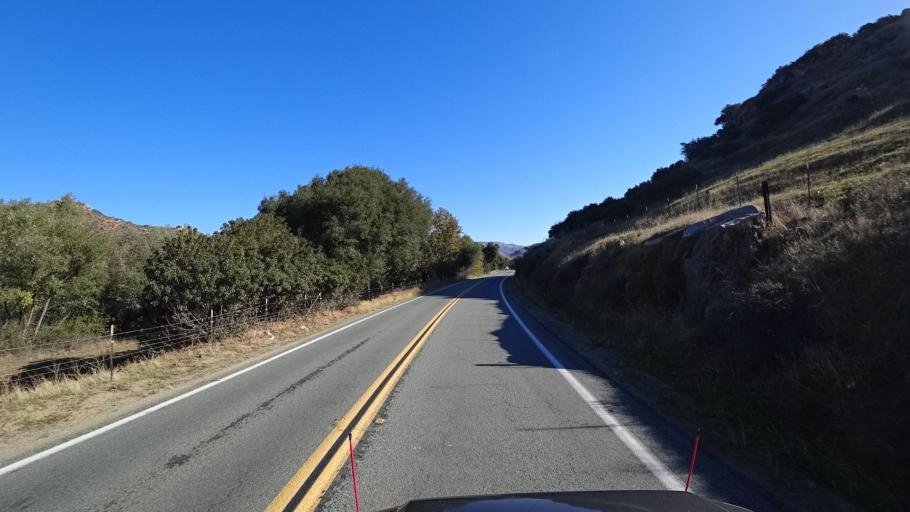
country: US
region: California
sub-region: San Diego County
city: Jamul
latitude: 32.6638
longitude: -116.8373
